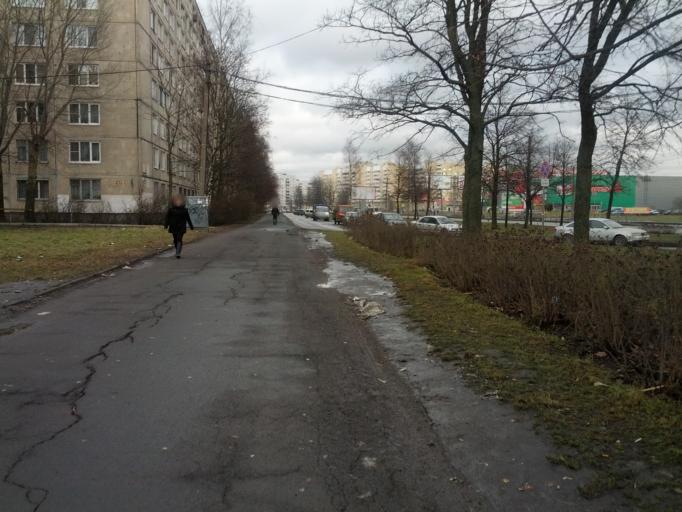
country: RU
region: Leningrad
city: Rybatskoye
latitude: 59.8933
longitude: 30.4904
